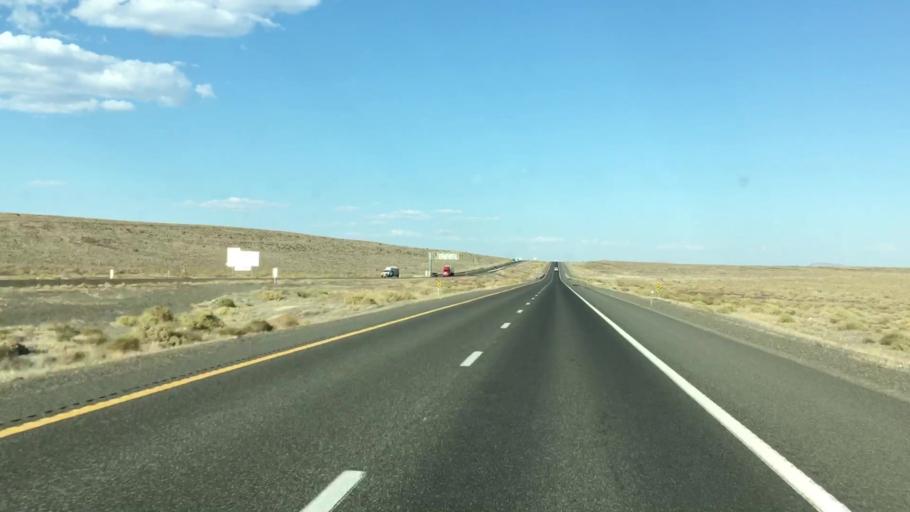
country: US
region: Nevada
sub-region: Pershing County
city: Lovelock
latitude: 39.9502
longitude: -118.7295
